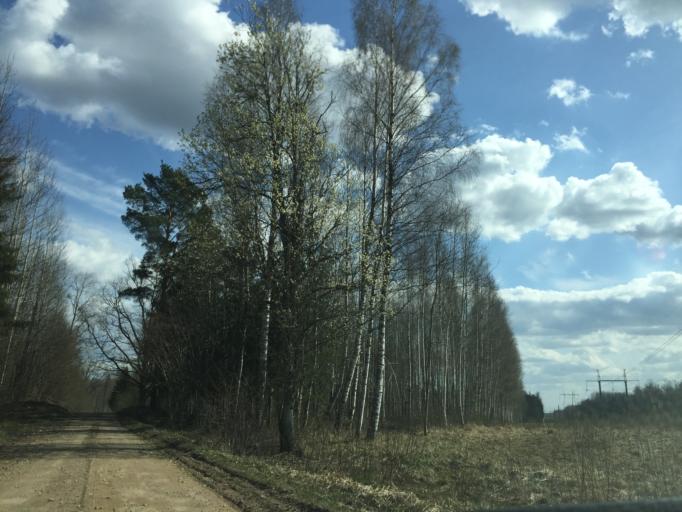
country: LV
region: Skriveri
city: Skriveri
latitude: 56.7986
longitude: 25.1637
